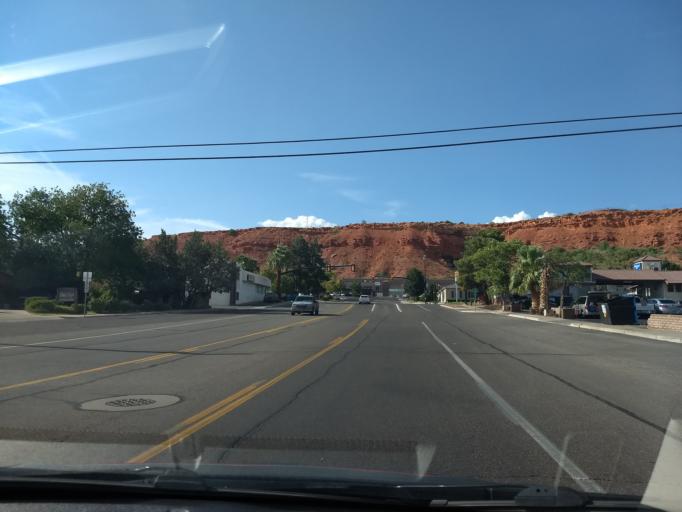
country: US
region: Utah
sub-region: Washington County
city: Saint George
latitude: 37.1089
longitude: -113.5748
